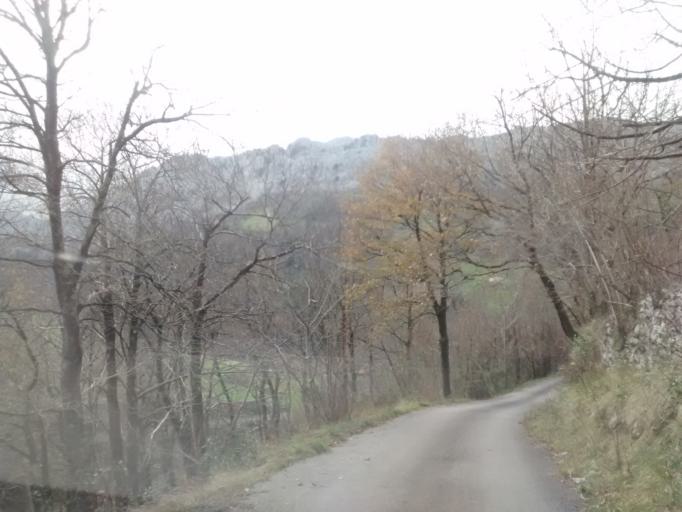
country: ES
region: Cantabria
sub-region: Provincia de Cantabria
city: Lierganes
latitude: 43.3226
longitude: -3.7097
